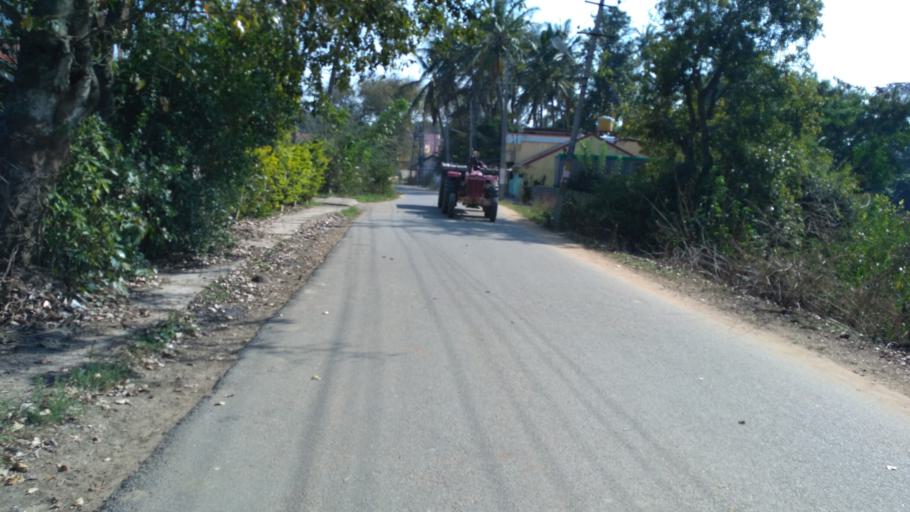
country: IN
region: Karnataka
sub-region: Hassan
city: Hassan
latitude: 13.0004
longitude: 76.1165
